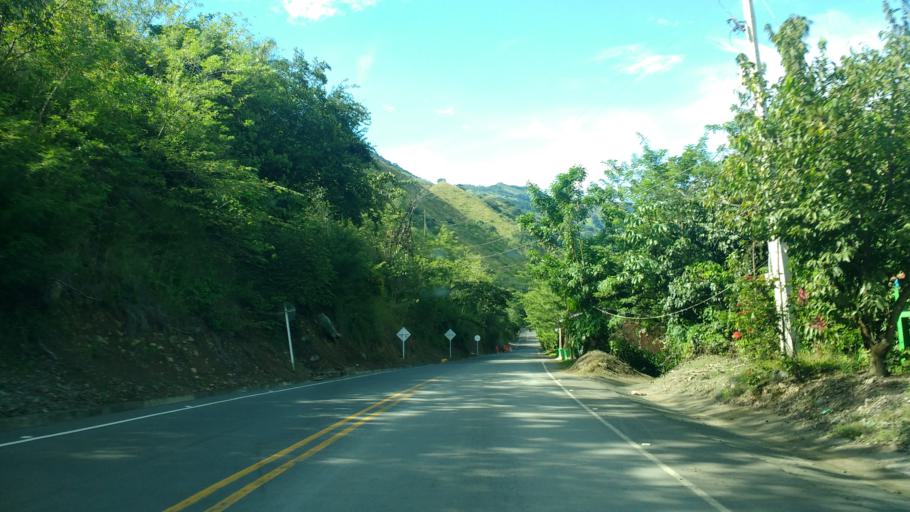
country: CO
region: Antioquia
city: Concordia
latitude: 6.0422
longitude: -75.8632
